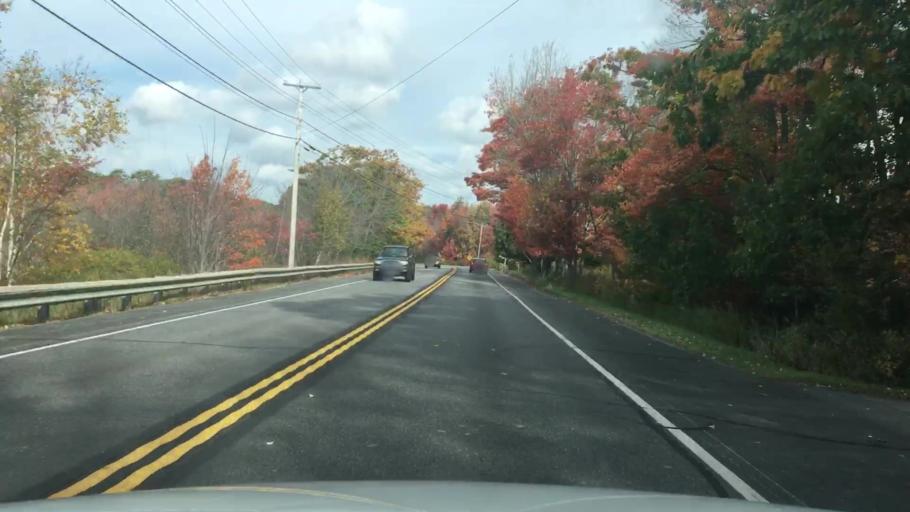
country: US
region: Maine
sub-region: Knox County
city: Rockport
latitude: 44.1702
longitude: -69.1199
